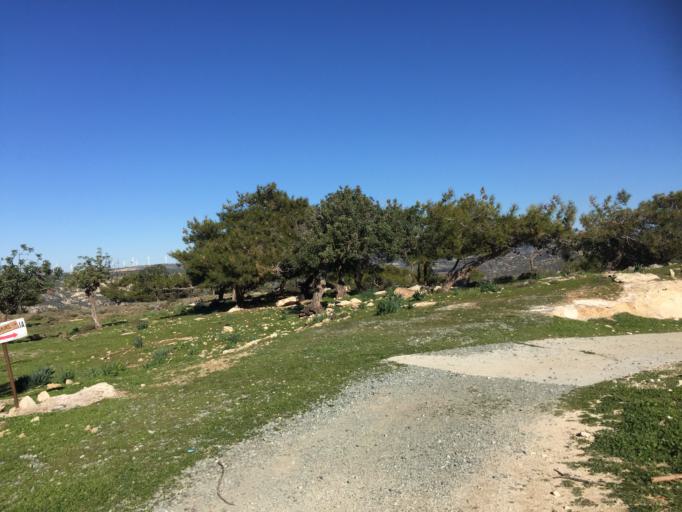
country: CY
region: Limassol
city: Pissouri
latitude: 34.6675
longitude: 32.6853
